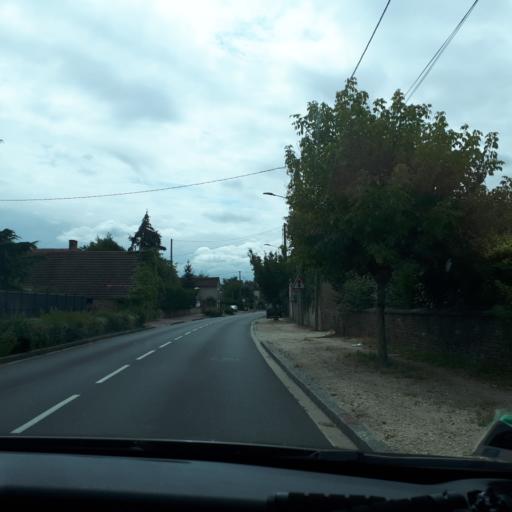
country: FR
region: Centre
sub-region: Departement du Loiret
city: Saint-Pere-sur-Loire
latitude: 47.7762
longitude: 2.3732
